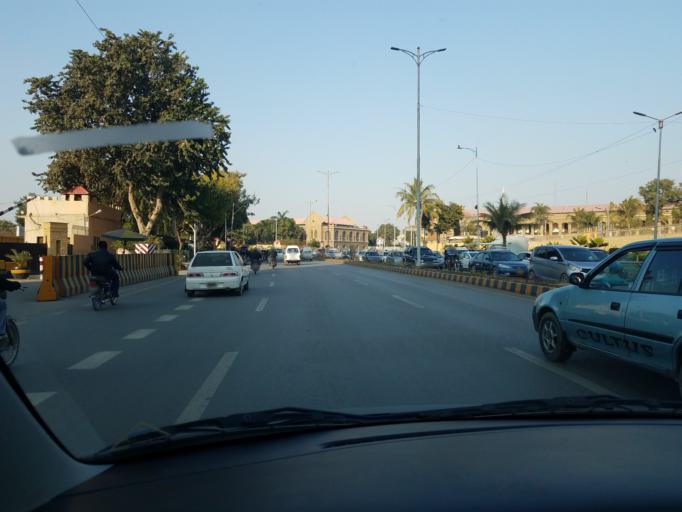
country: PK
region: Sindh
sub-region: Karachi District
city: Karachi
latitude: 24.8537
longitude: 67.0353
